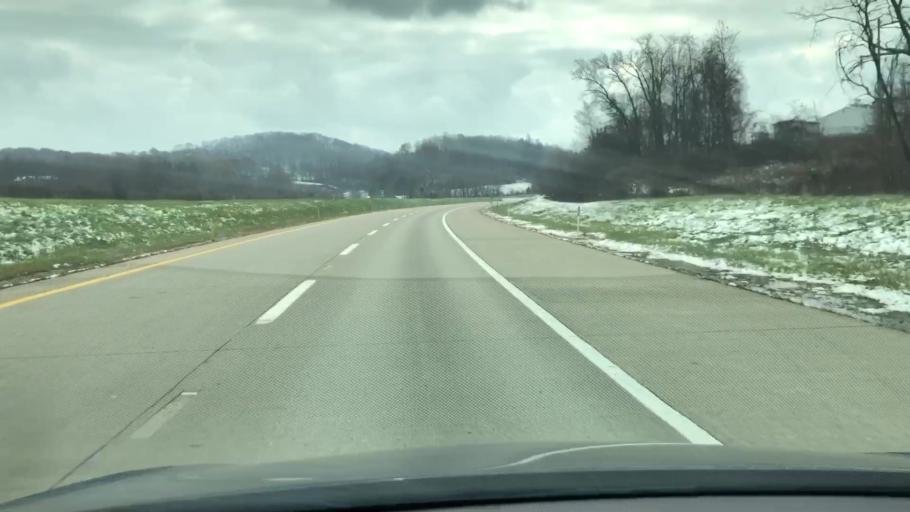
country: US
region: Pennsylvania
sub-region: Westmoreland County
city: Delmont
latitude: 40.3672
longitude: -79.5569
